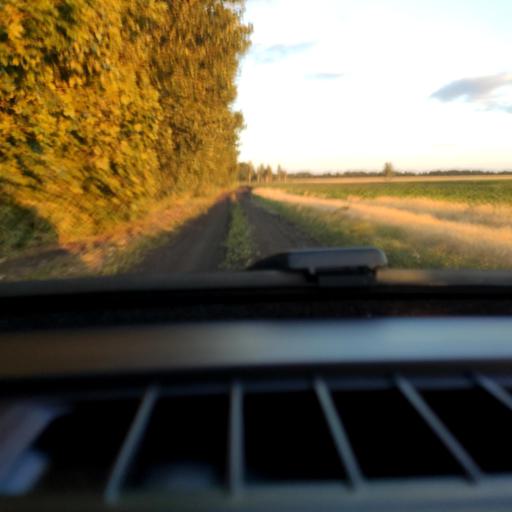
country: RU
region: Voronezj
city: Panino
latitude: 51.5743
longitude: 39.8787
